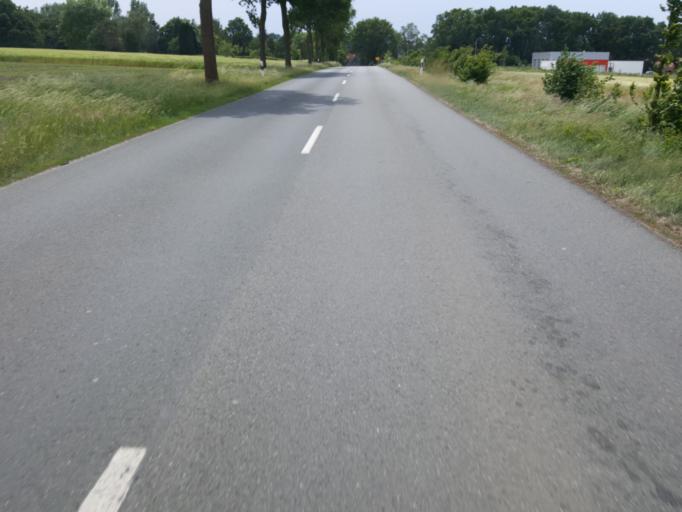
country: DE
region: Lower Saxony
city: Husum
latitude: 52.5715
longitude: 9.2486
